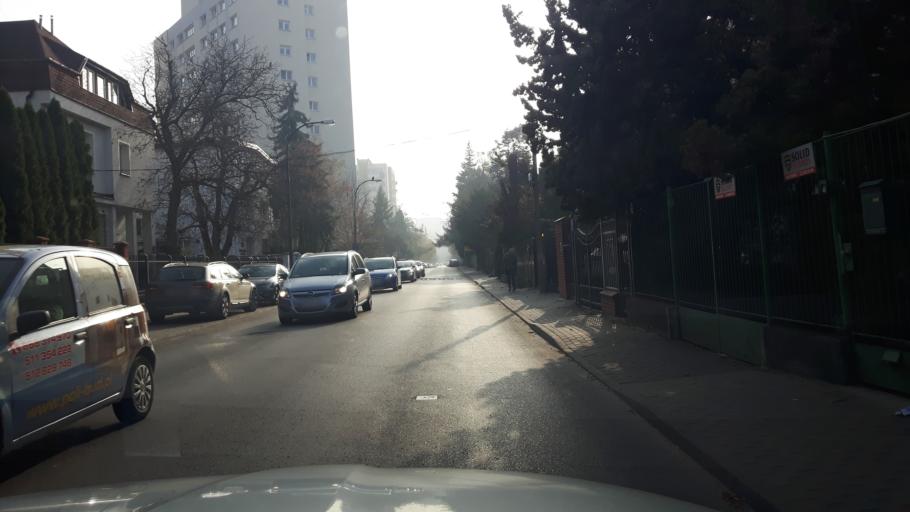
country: PL
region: Masovian Voivodeship
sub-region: Warszawa
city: Ochota
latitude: 52.1947
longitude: 20.9918
